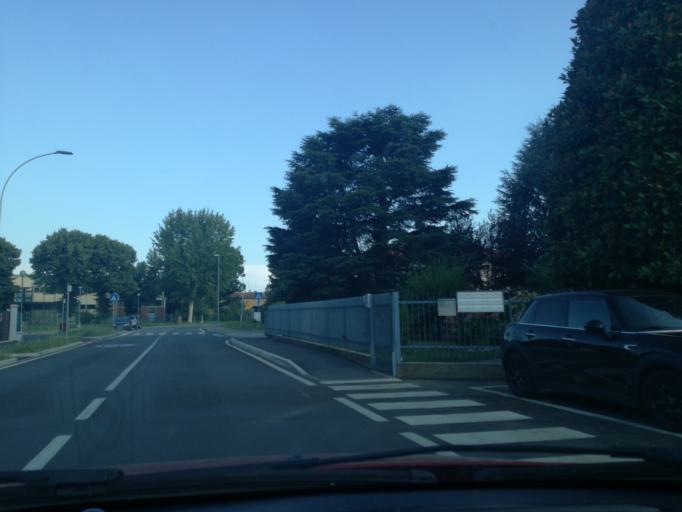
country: IT
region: Lombardy
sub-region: Provincia di Monza e Brianza
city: Arcore
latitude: 45.6325
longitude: 9.3266
